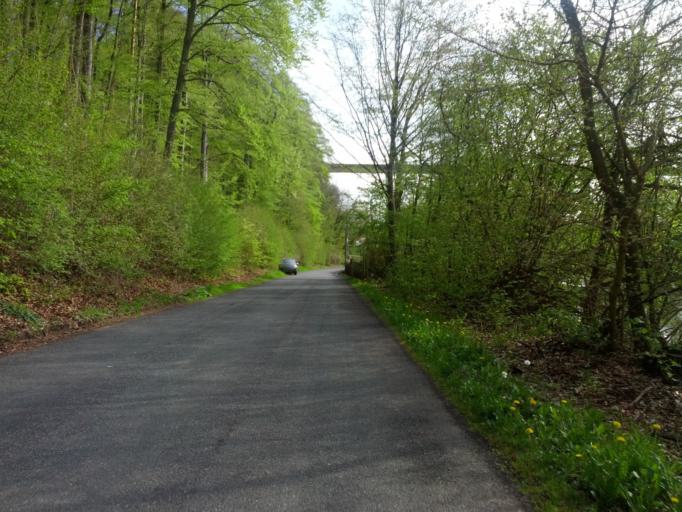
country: DE
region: Thuringia
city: Krauthausen
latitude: 51.0148
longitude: 10.2360
